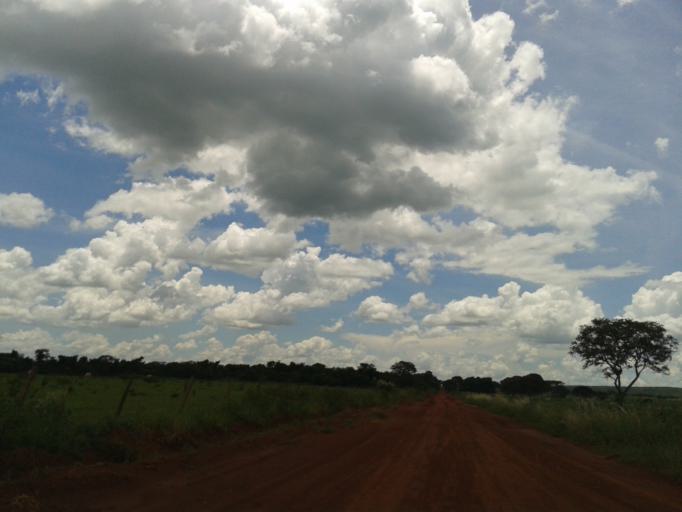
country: BR
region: Minas Gerais
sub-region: Ituiutaba
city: Ituiutaba
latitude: -18.8905
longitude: -49.4665
